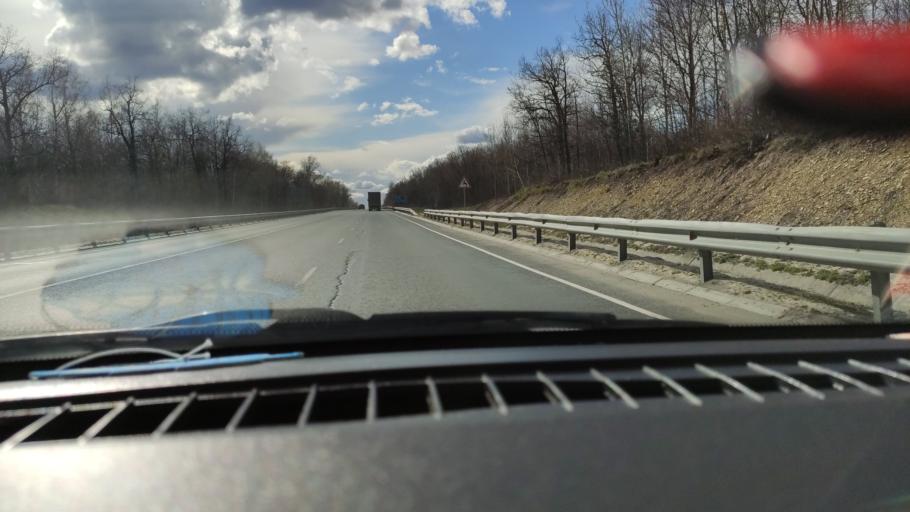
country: RU
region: Saratov
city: Vol'sk
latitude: 52.1098
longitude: 47.3647
